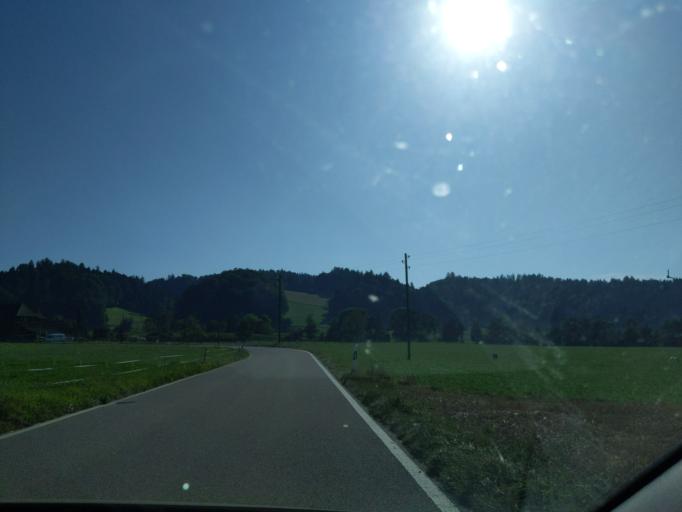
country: CH
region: Bern
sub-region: Oberaargau
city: Rohrbach
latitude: 47.1319
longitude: 7.8086
